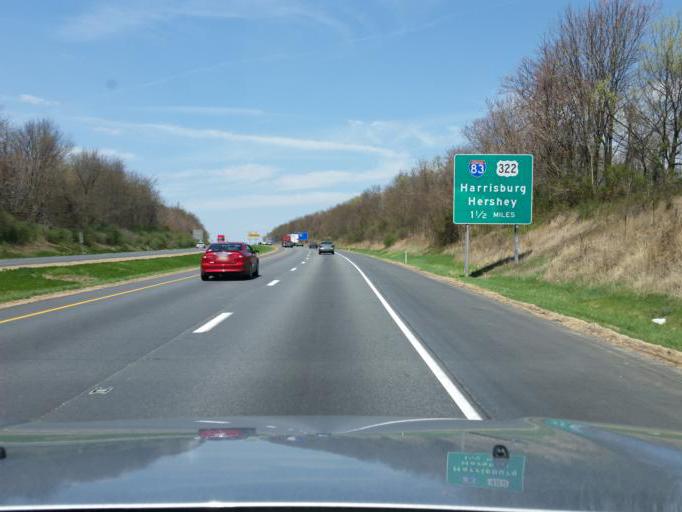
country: US
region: Pennsylvania
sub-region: Dauphin County
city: Highspire
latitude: 40.2328
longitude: -76.7965
